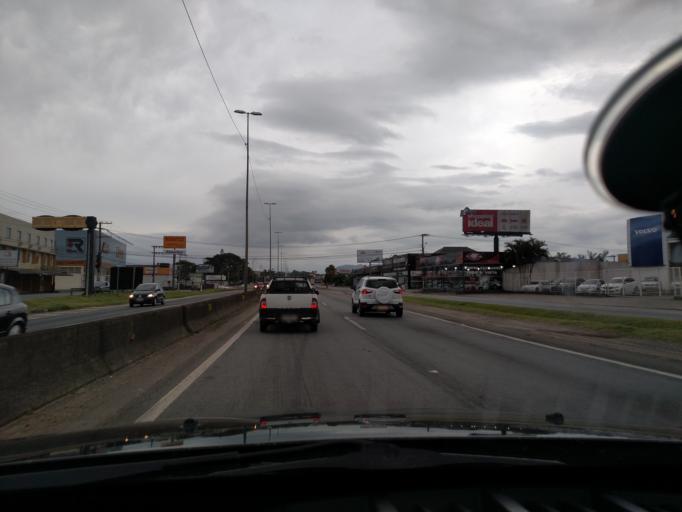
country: BR
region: Santa Catarina
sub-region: Sao Jose
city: Campinas
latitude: -27.5637
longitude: -48.6152
